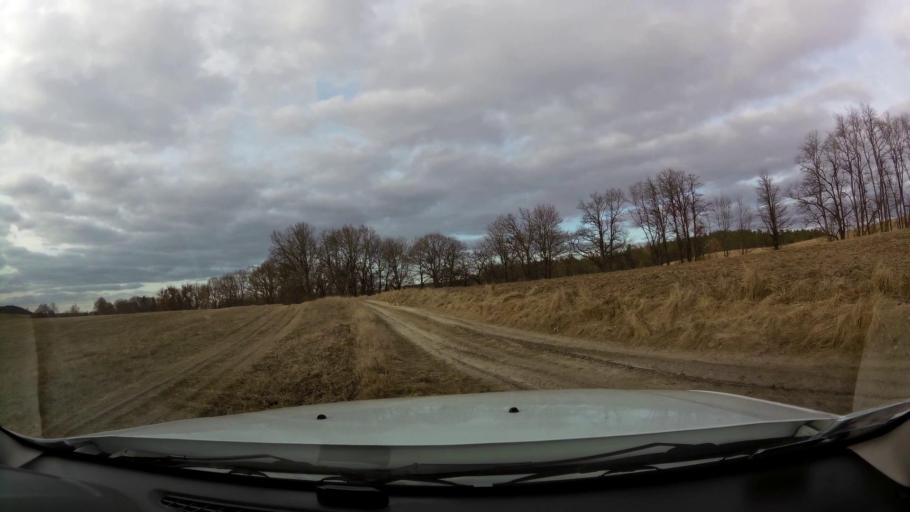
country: PL
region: West Pomeranian Voivodeship
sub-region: Powiat drawski
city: Drawsko Pomorskie
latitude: 53.5176
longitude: 15.7116
